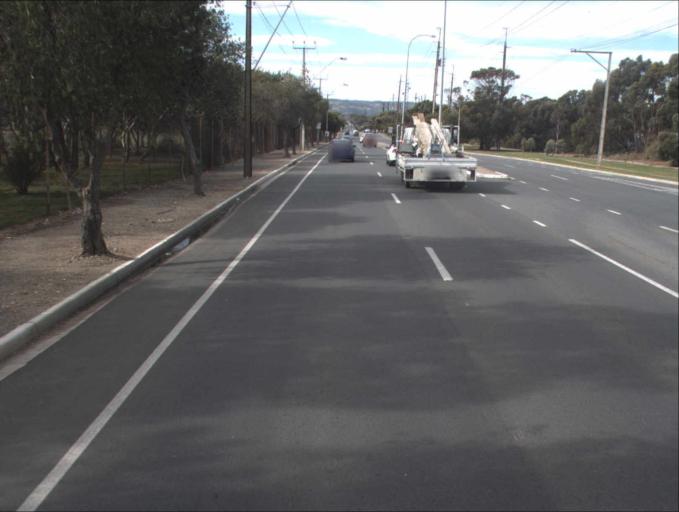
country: AU
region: South Australia
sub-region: Salisbury
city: Ingle Farm
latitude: -34.8471
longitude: 138.6290
